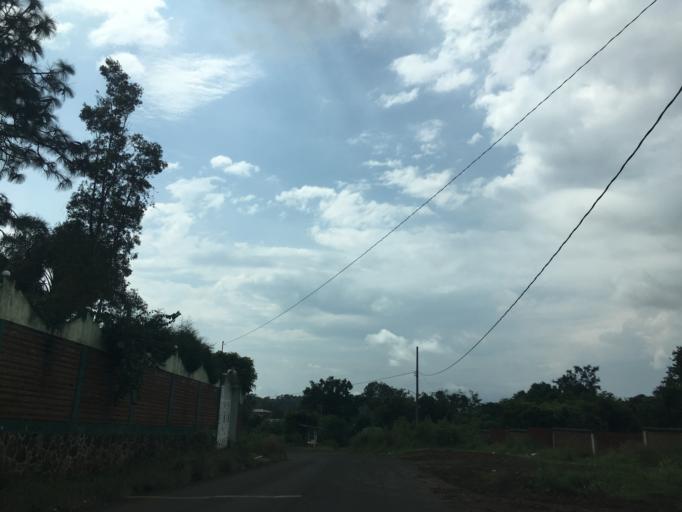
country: MX
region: Michoacan
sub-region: Periban
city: San Francisco Periban
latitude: 19.5839
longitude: -102.4238
